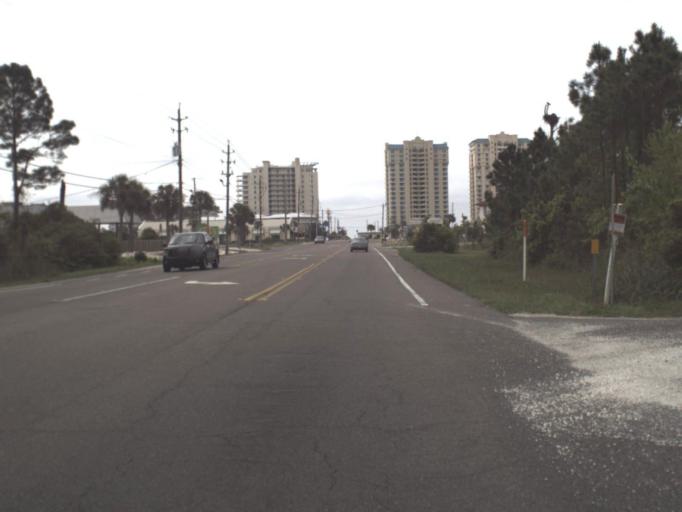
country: US
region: Alabama
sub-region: Baldwin County
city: Orange Beach
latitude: 30.3029
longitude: -87.4274
